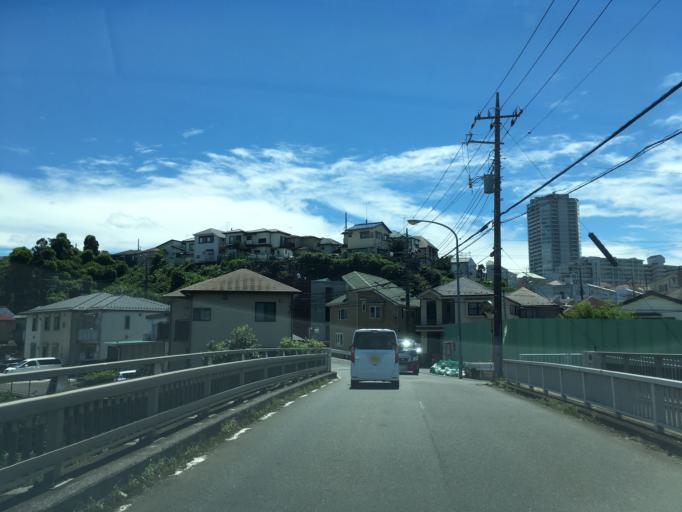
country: JP
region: Tokyo
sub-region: Machida-shi
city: Machida
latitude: 35.5370
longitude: 139.4985
